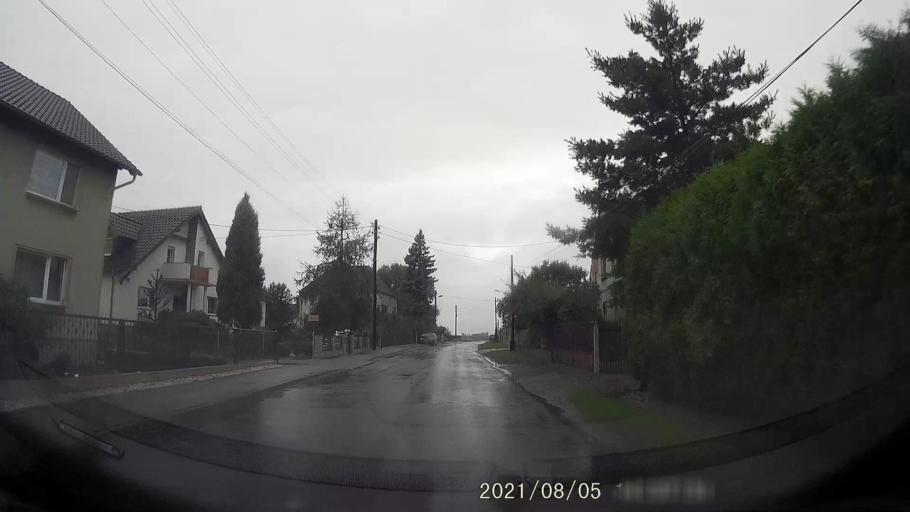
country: PL
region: Opole Voivodeship
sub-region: Powiat krapkowicki
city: Strzeleczki
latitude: 50.4681
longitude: 17.8242
